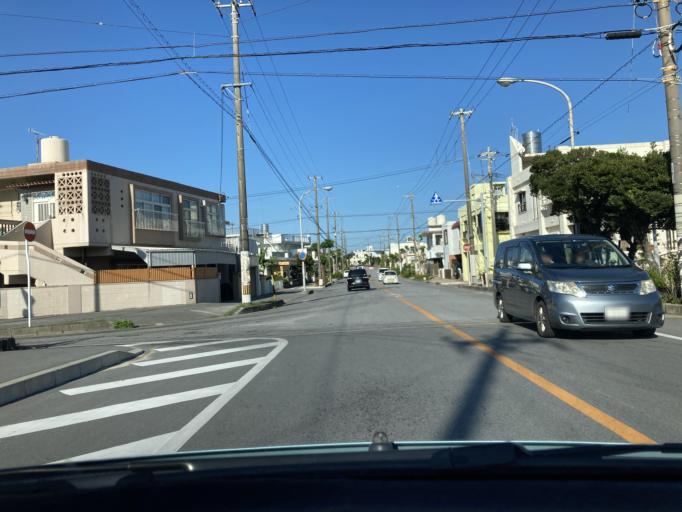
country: JP
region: Okinawa
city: Chatan
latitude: 26.2853
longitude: 127.7842
